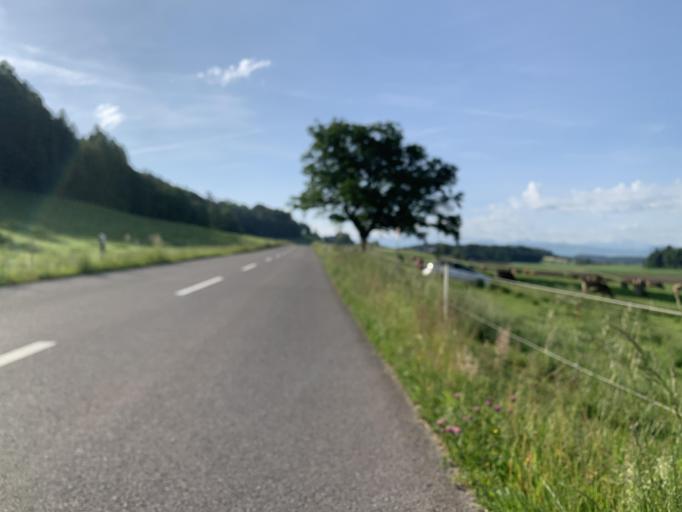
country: CH
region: Zurich
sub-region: Bezirk Uster
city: Uster / Nossikon
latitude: 47.3317
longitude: 8.7285
